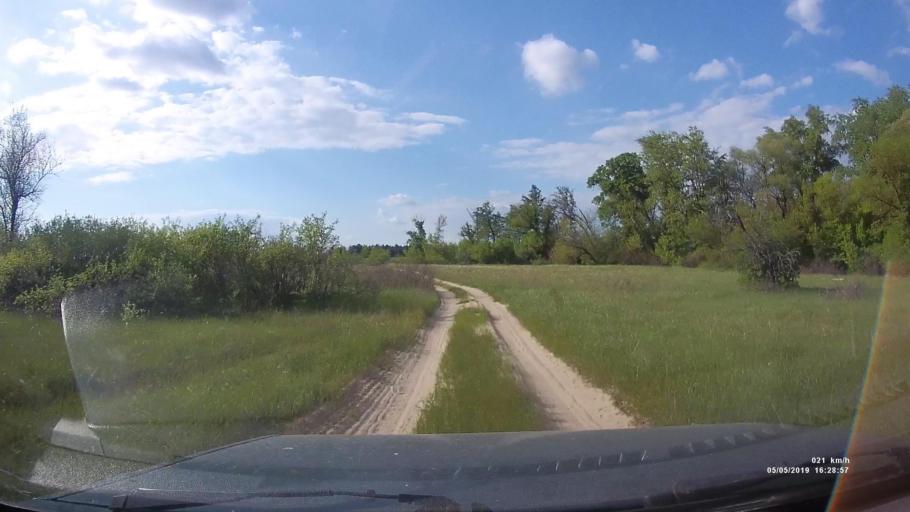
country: RU
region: Rostov
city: Ust'-Donetskiy
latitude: 47.7691
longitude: 41.0152
